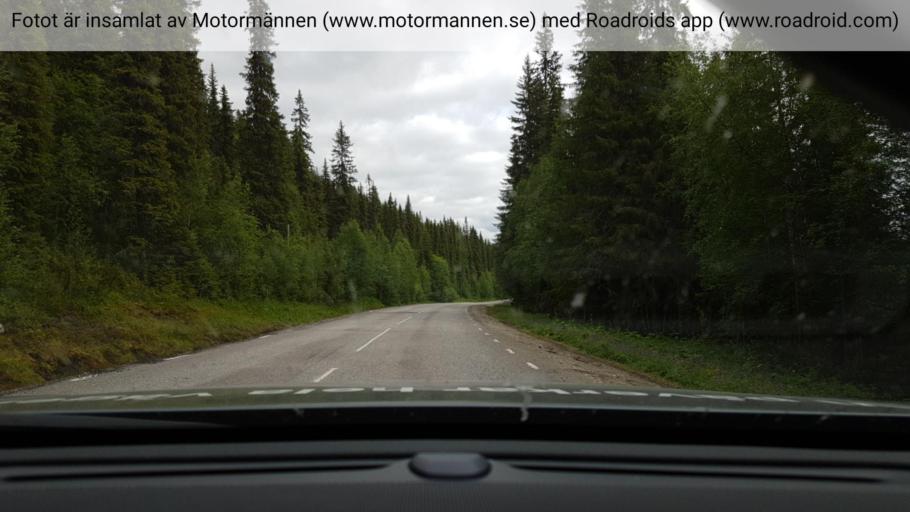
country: SE
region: Vaesterbotten
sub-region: Storumans Kommun
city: Fristad
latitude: 65.8192
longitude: 16.8459
